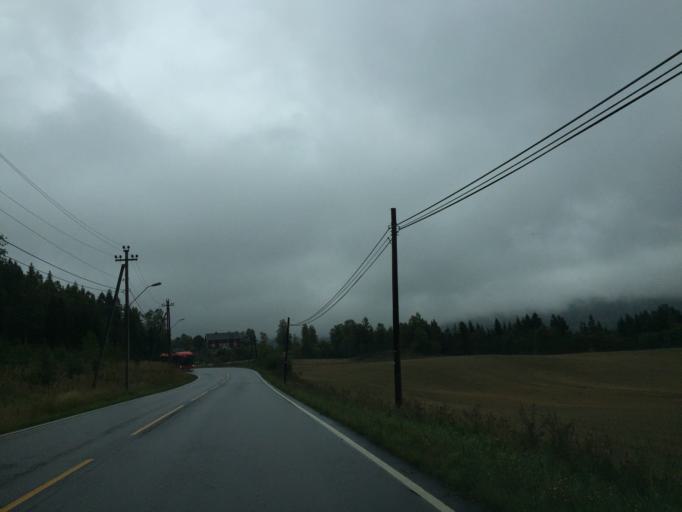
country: NO
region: Akershus
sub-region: Baerum
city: Lysaker
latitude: 60.0030
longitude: 10.6190
